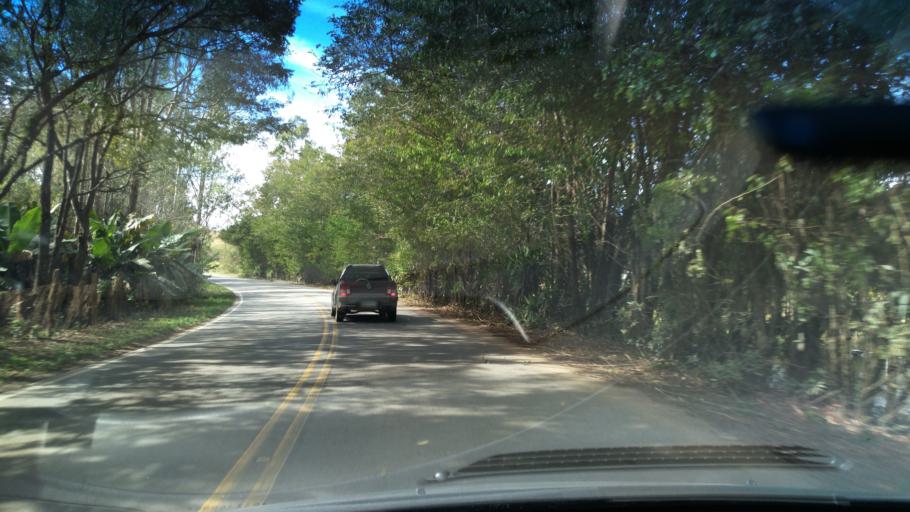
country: BR
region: Minas Gerais
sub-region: Andradas
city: Andradas
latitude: -22.0660
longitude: -46.4676
